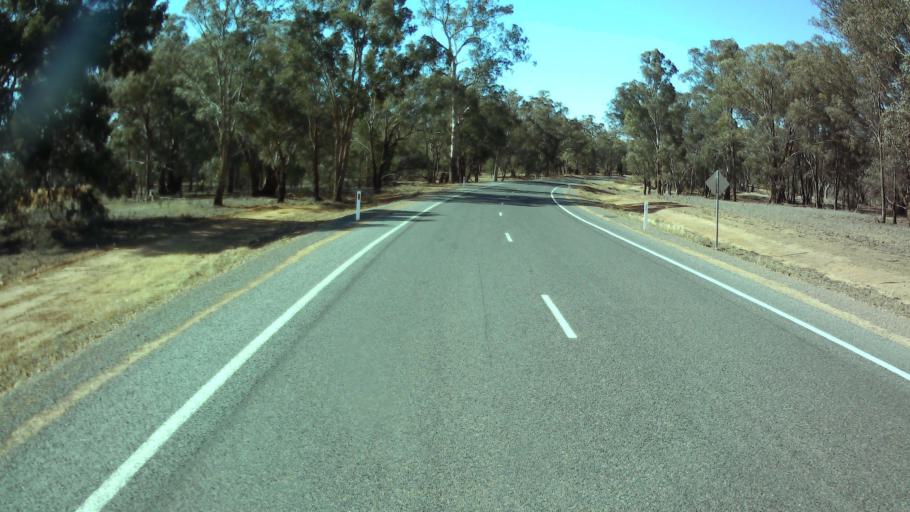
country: AU
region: New South Wales
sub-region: Weddin
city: Grenfell
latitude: -33.7643
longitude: 148.0820
